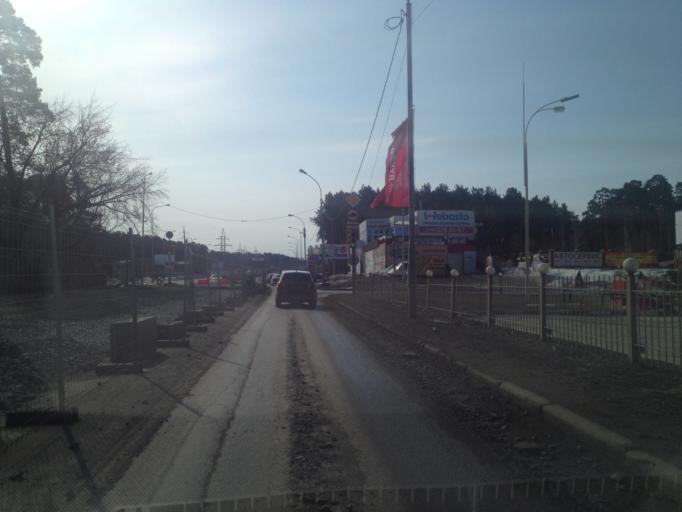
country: RU
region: Sverdlovsk
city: Sovkhoznyy
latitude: 56.7967
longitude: 60.5956
